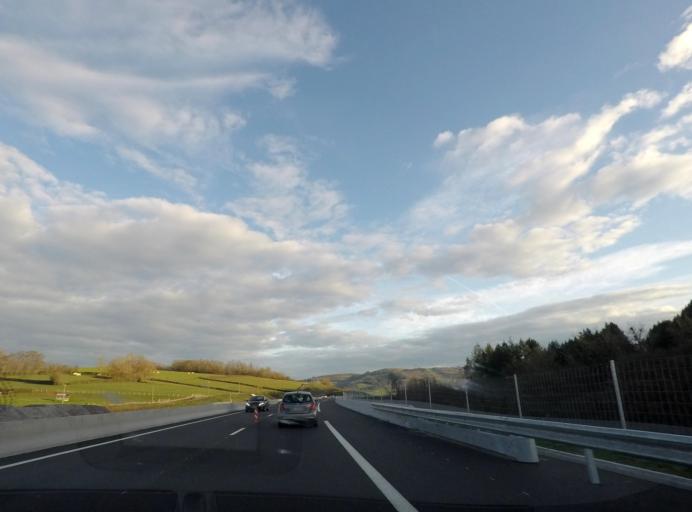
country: FR
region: Bourgogne
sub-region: Departement de Saone-et-Loire
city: Matour
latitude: 46.3716
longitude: 4.5496
